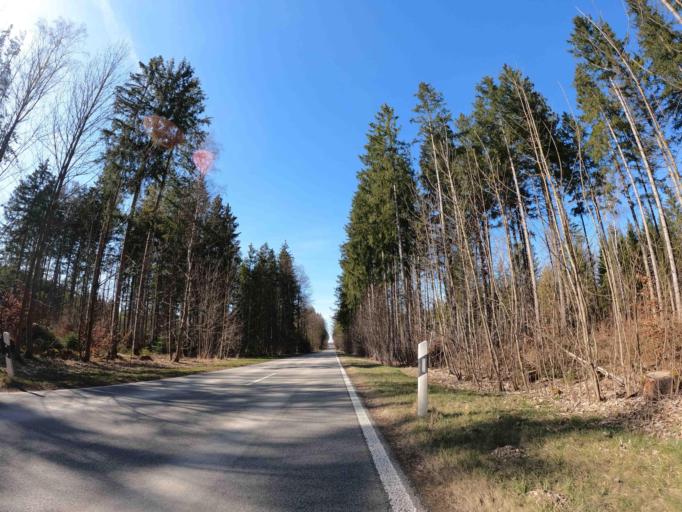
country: DE
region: Bavaria
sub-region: Upper Bavaria
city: Oberhaching
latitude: 48.0102
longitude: 11.6167
